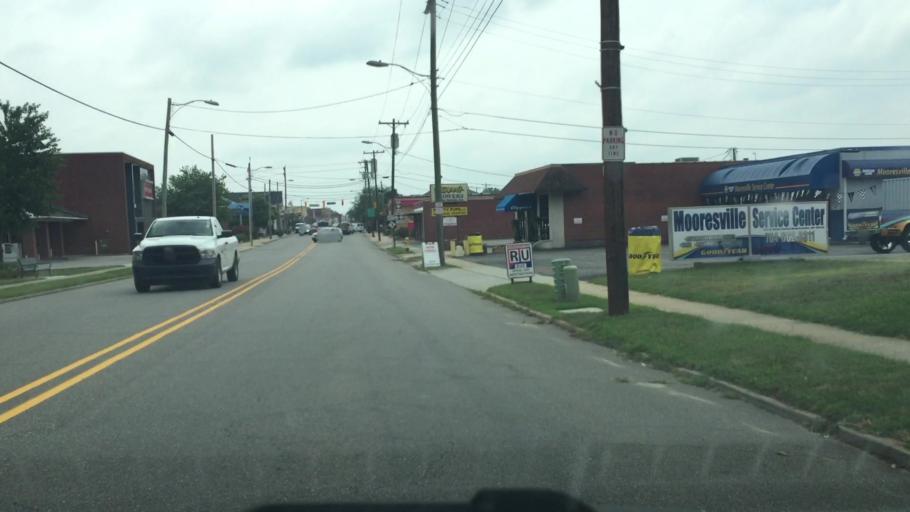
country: US
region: North Carolina
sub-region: Iredell County
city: Mooresville
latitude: 35.5858
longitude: -80.8084
